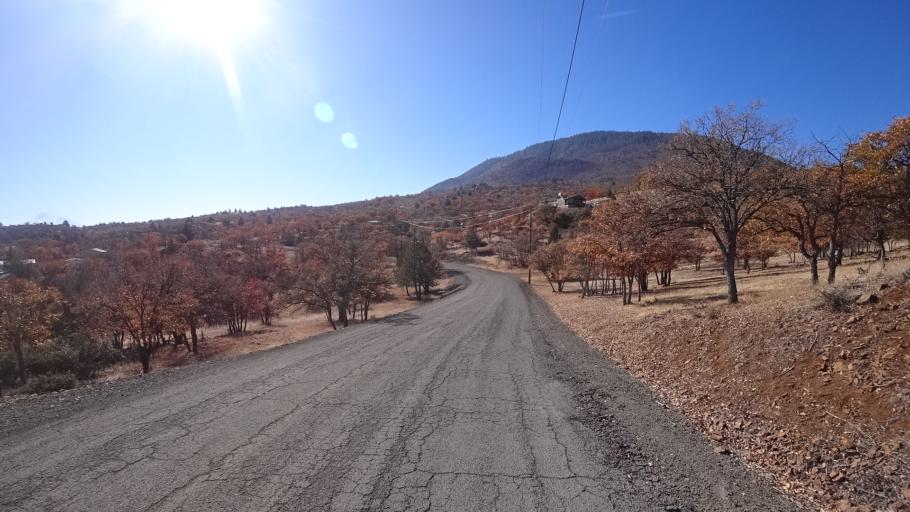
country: US
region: California
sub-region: Siskiyou County
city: Montague
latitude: 41.8753
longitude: -122.4837
